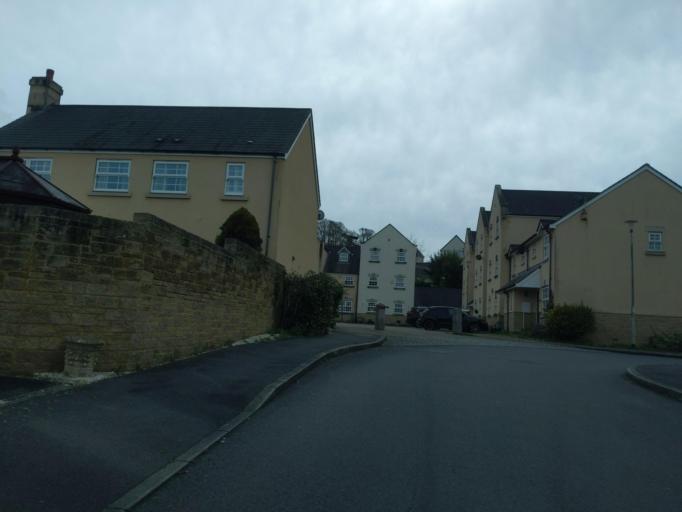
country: GB
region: England
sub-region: Plymouth
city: Plymouth
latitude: 50.4074
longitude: -4.1431
